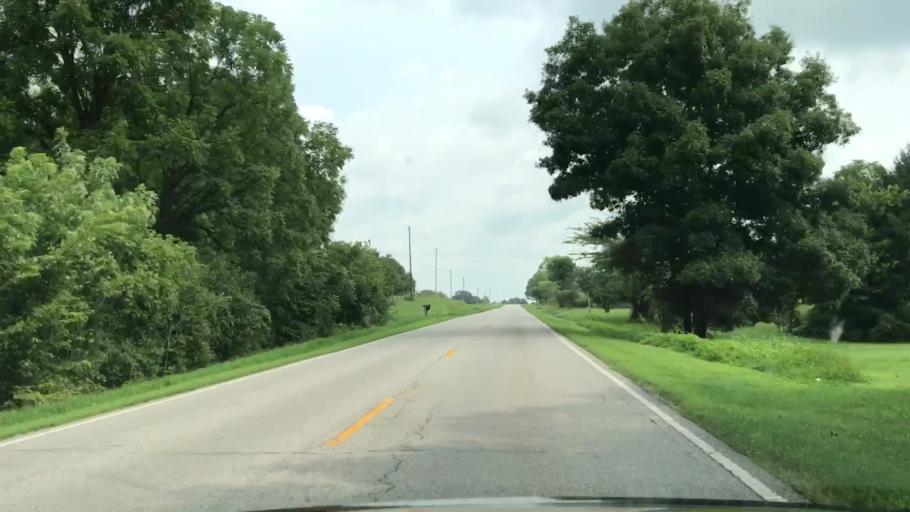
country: US
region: Kentucky
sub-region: Barren County
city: Cave City
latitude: 37.1043
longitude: -86.0014
